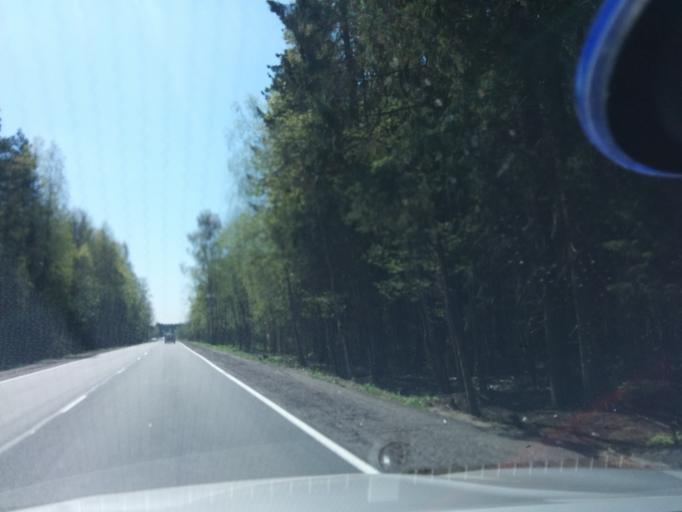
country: RU
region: Leningrad
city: Verkhniye Osel'ki
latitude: 60.2084
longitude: 30.4264
